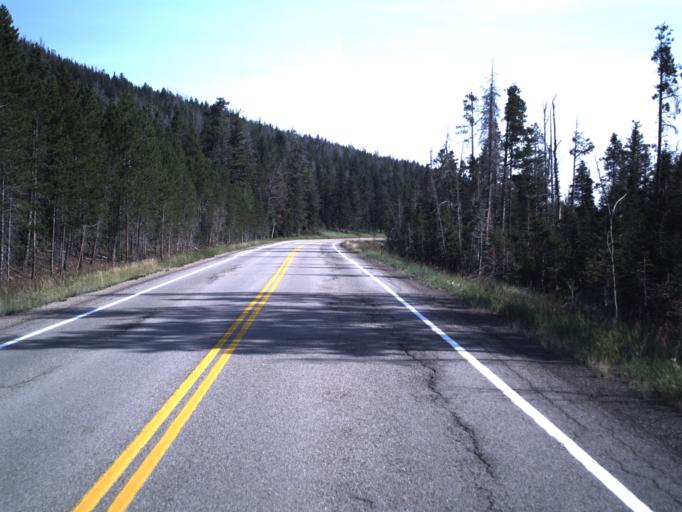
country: US
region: Utah
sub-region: Daggett County
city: Manila
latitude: 40.8168
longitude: -109.4662
